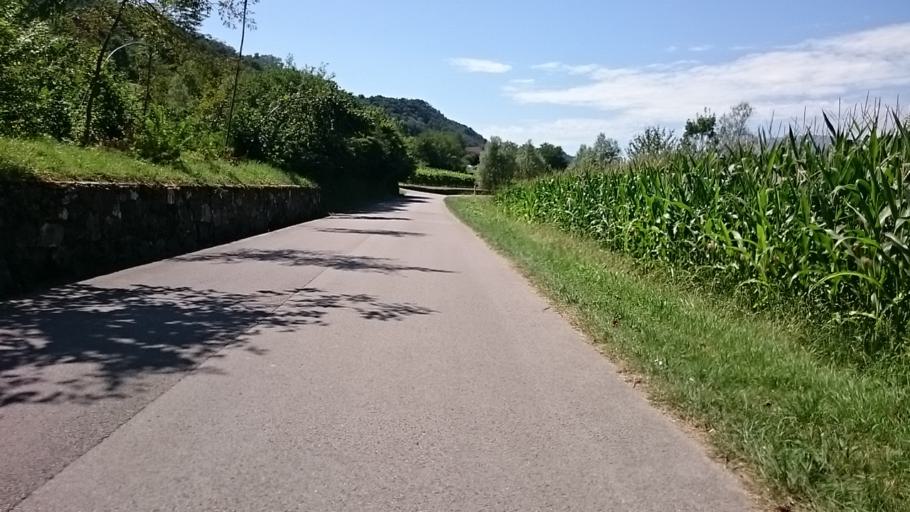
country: IT
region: Veneto
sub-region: Provincia di Treviso
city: Tarzo
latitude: 45.9809
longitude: 12.2281
